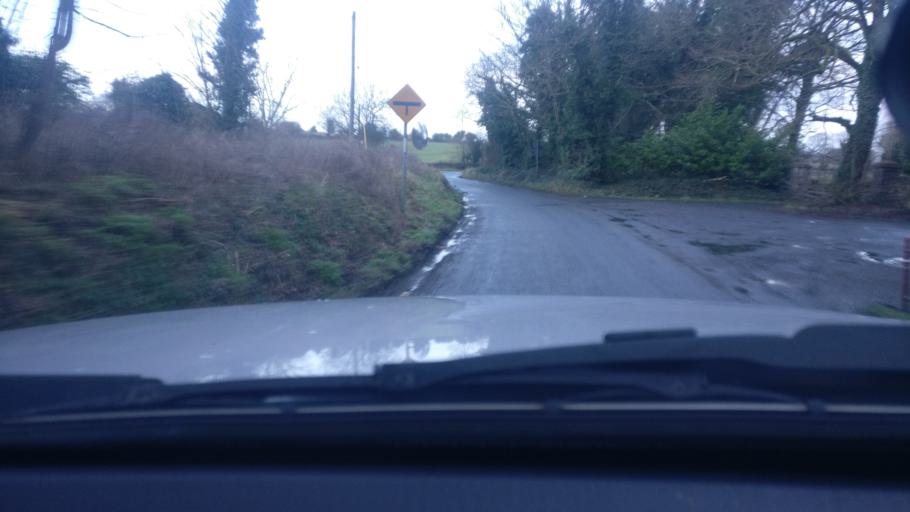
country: IE
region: Connaught
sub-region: County Galway
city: Loughrea
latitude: 53.1892
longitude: -8.6020
